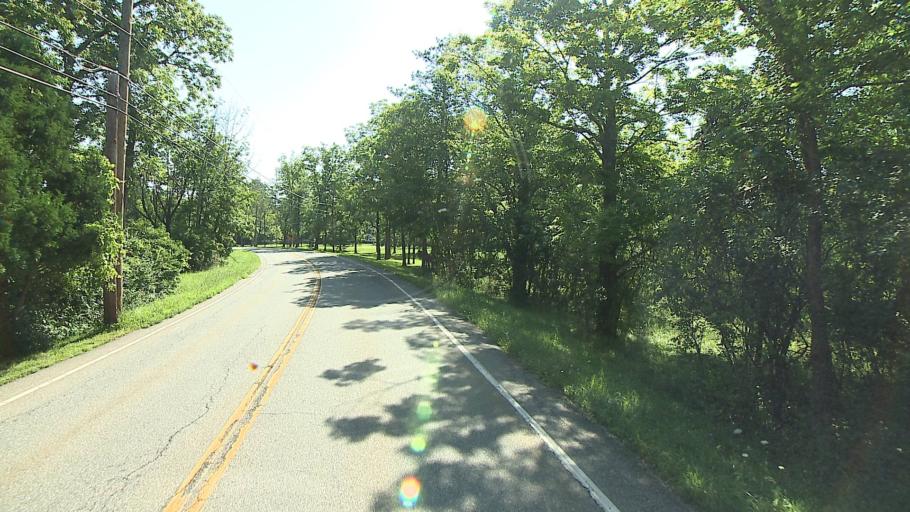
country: US
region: Connecticut
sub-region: Litchfield County
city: Kent
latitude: 41.8624
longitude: -73.4807
